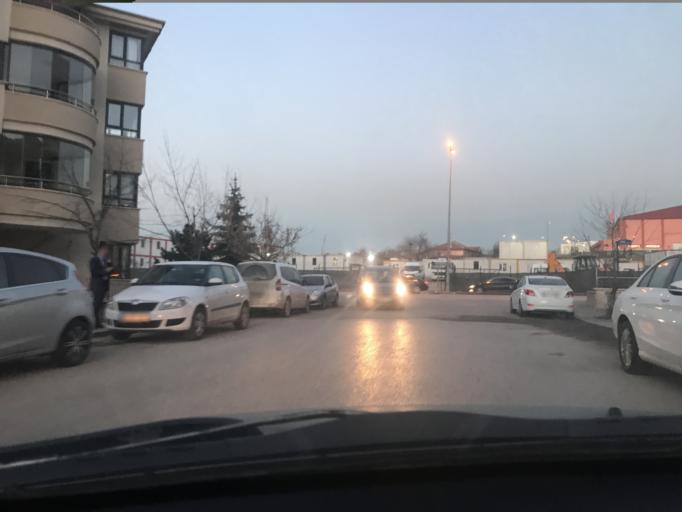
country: TR
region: Ankara
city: Batikent
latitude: 39.9146
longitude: 32.7726
